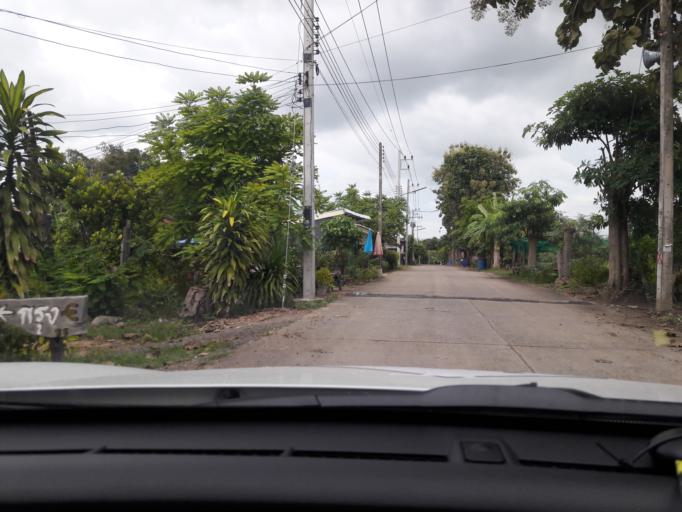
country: TH
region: Nakhon Sawan
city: Tak Fa
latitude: 15.3531
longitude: 100.4945
